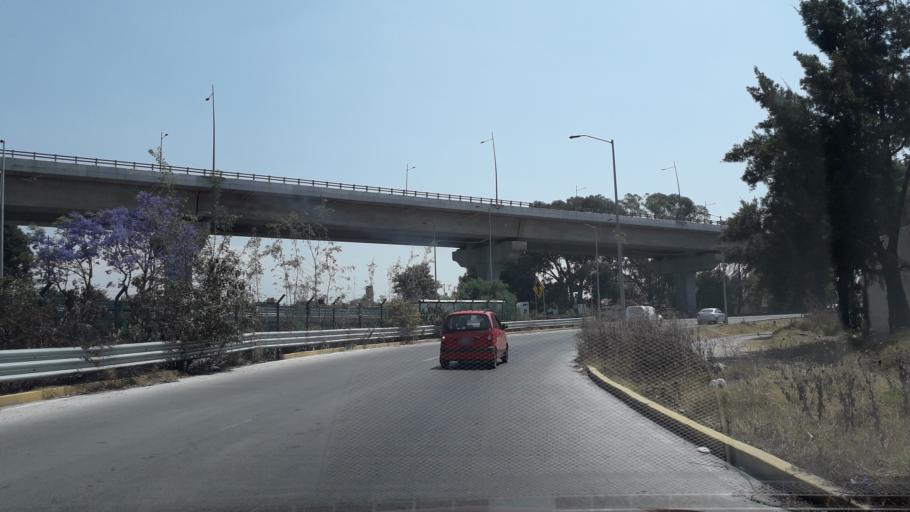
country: MX
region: Puebla
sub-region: Cuautlancingo
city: Sanctorum
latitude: 19.0957
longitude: -98.2286
